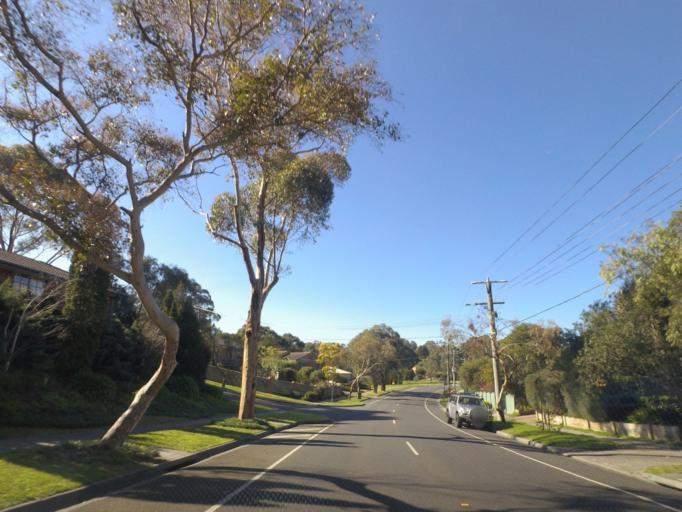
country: AU
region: Victoria
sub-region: Maroondah
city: Croydon Hills
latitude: -37.7764
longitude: 145.2584
